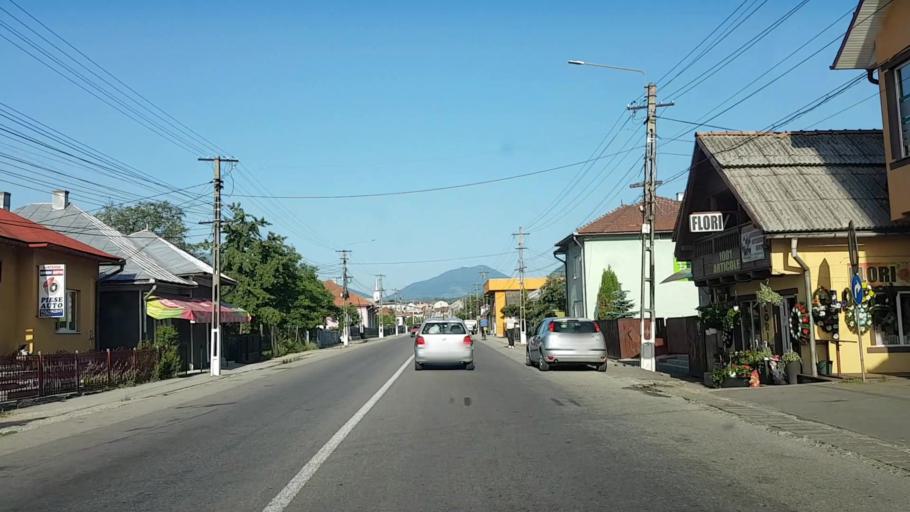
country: RO
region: Bistrita-Nasaud
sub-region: Comuna Prundu Bargaului
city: Susenii Bargaului
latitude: 47.2202
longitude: 24.7303
